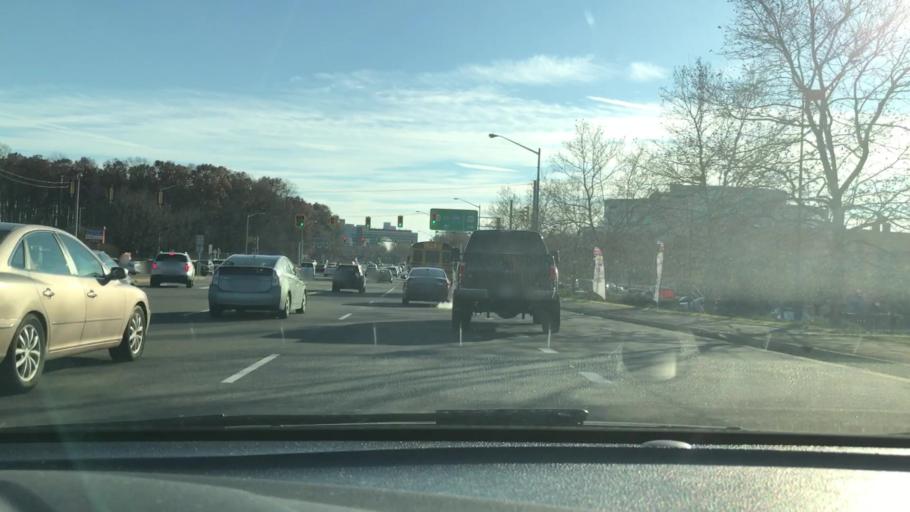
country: US
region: Virginia
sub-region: Fairfax County
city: Merrifield
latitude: 38.8675
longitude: -77.2278
